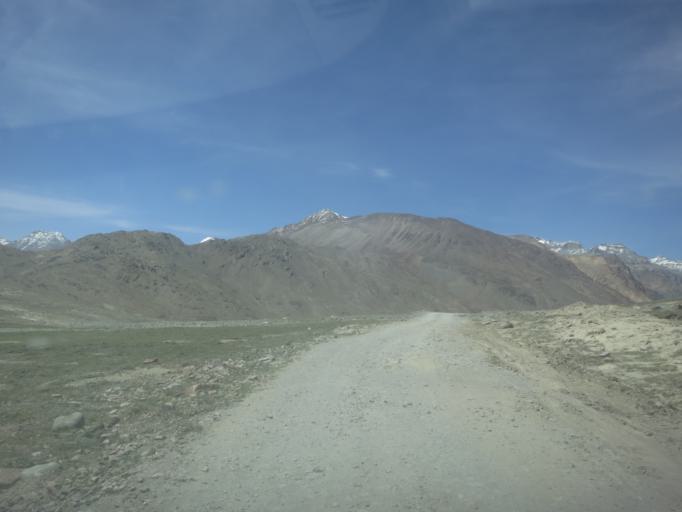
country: IN
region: Himachal Pradesh
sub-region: Kulu
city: Manali
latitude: 32.3954
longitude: 77.6353
